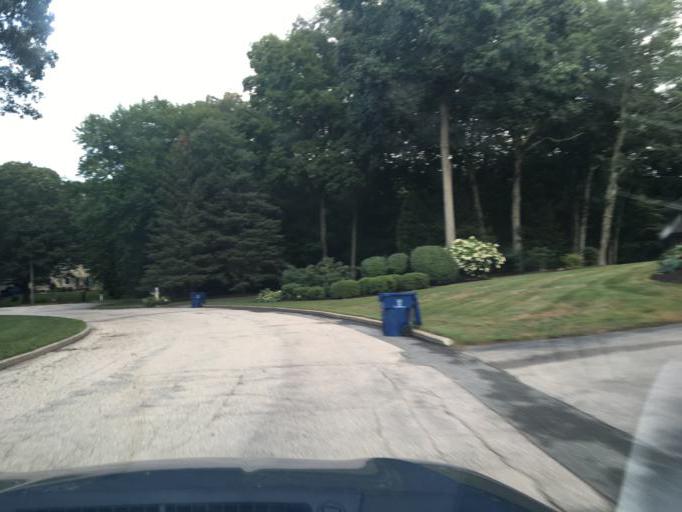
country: US
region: Rhode Island
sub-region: Kent County
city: East Greenwich
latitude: 41.6504
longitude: -71.5018
